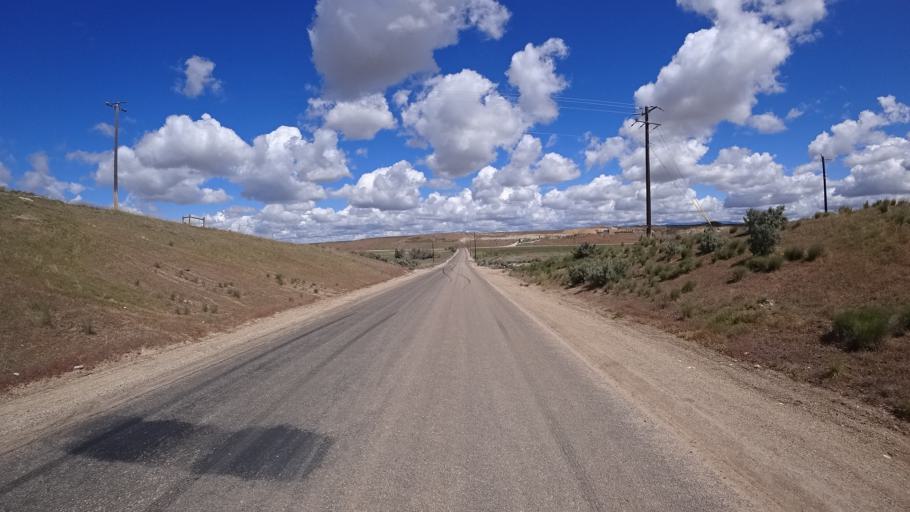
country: US
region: Idaho
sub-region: Ada County
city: Garden City
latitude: 43.4881
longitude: -116.2743
